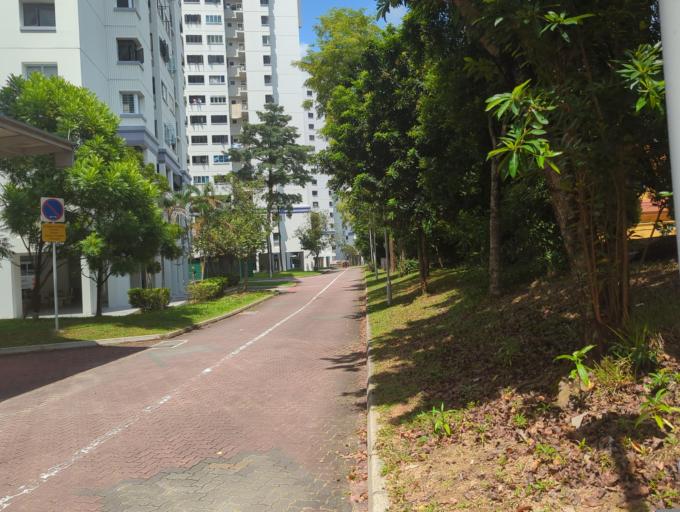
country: MY
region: Johor
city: Kampung Pasir Gudang Baru
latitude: 1.3923
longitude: 103.9002
